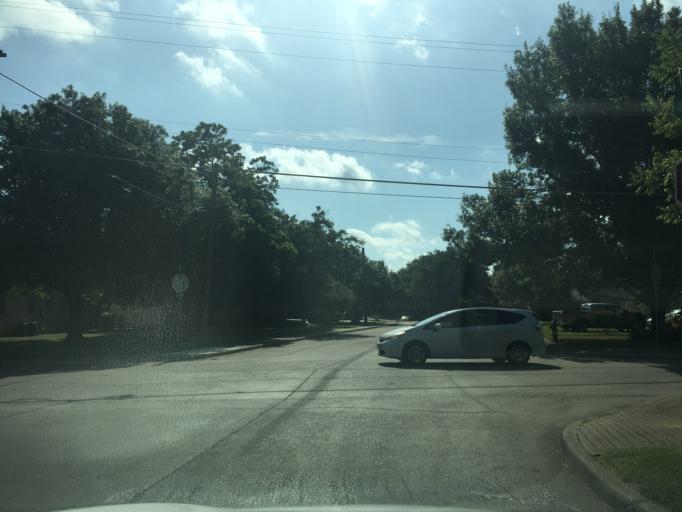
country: US
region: Texas
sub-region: Dallas County
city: Highland Park
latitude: 32.8357
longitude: -96.7585
